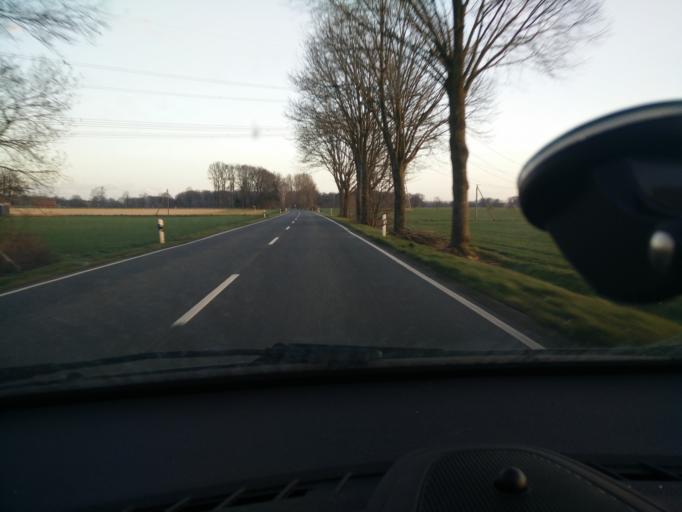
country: DE
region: North Rhine-Westphalia
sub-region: Regierungsbezirk Munster
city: Borken
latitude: 51.8206
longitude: 6.8651
